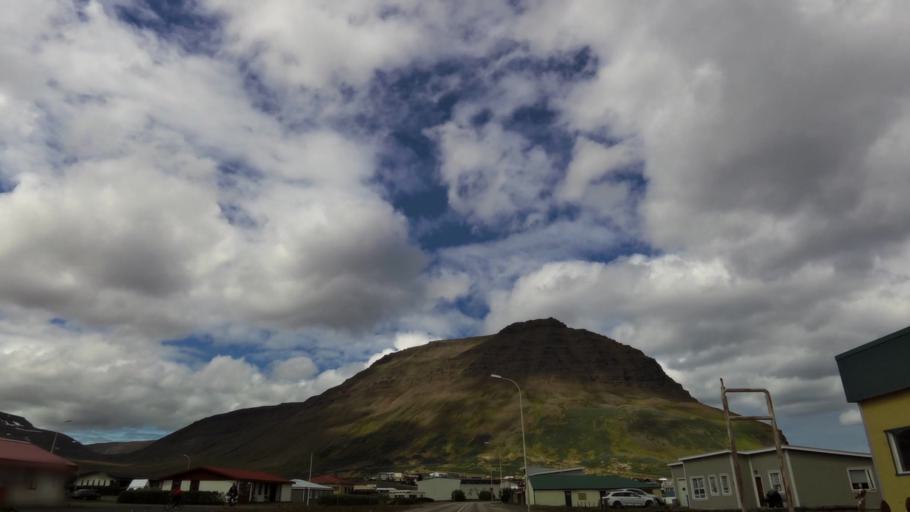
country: IS
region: Westfjords
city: Isafjoerdur
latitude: 66.1533
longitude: -23.2496
